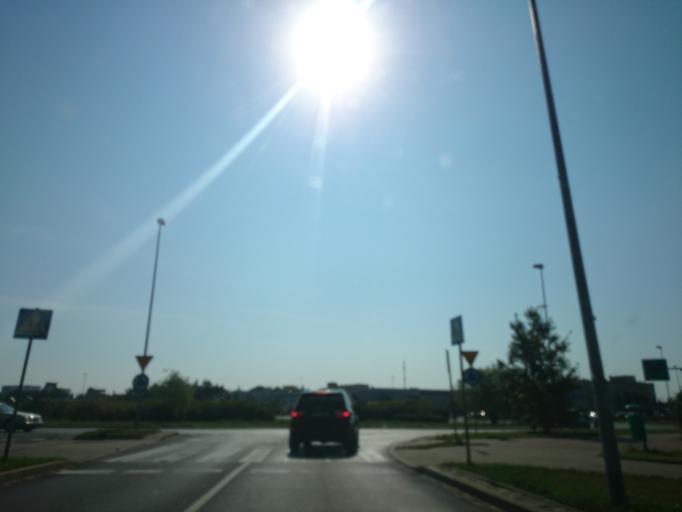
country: PL
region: West Pomeranian Voivodeship
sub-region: Powiat policki
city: Przeclaw
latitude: 53.4036
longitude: 14.5000
